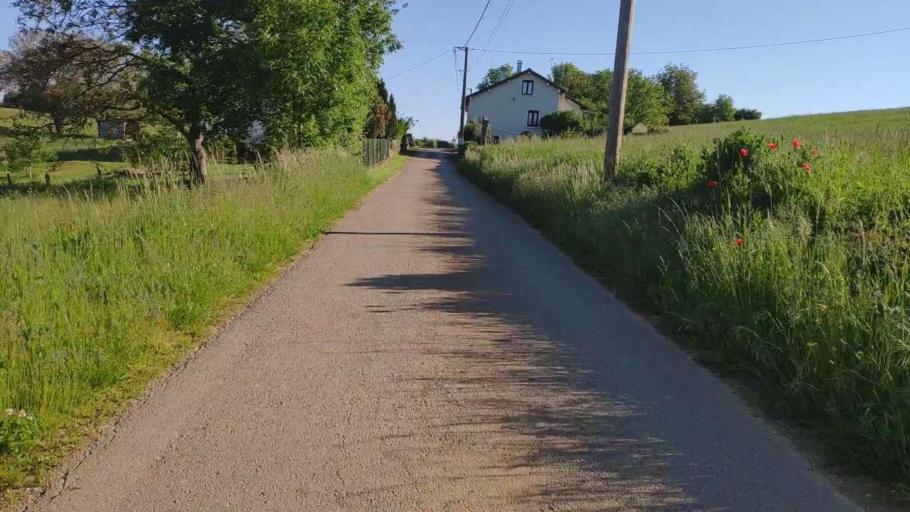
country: FR
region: Franche-Comte
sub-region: Departement du Jura
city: Perrigny
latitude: 46.7178
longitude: 5.6211
